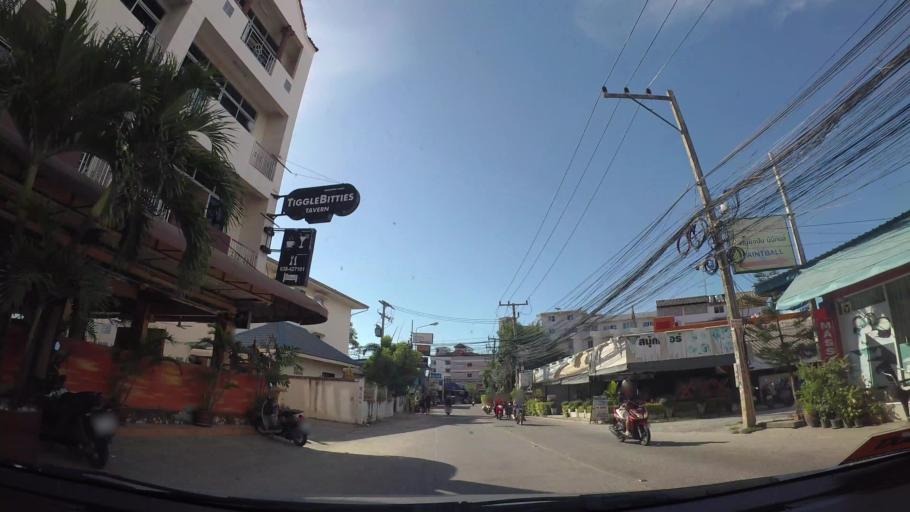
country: TH
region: Chon Buri
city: Phatthaya
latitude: 12.9168
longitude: 100.8793
